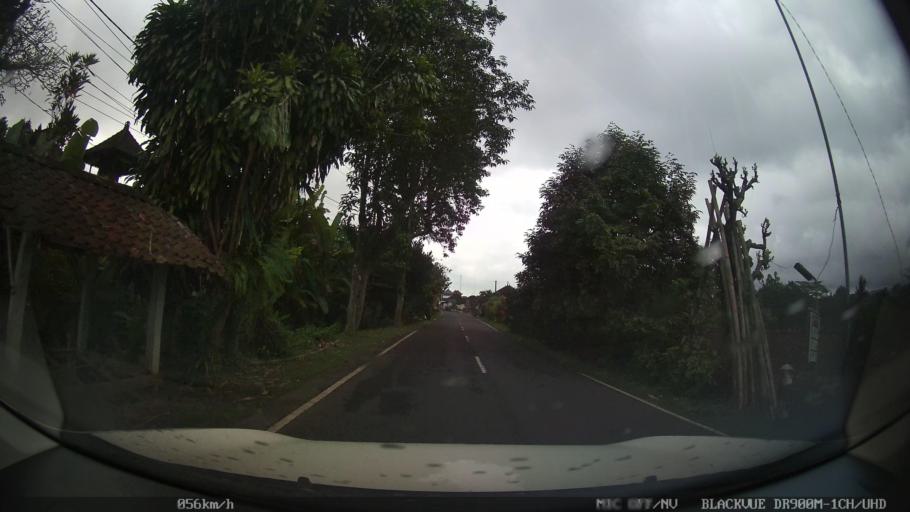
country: ID
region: Bali
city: Empalan
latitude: -8.3939
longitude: 115.1515
